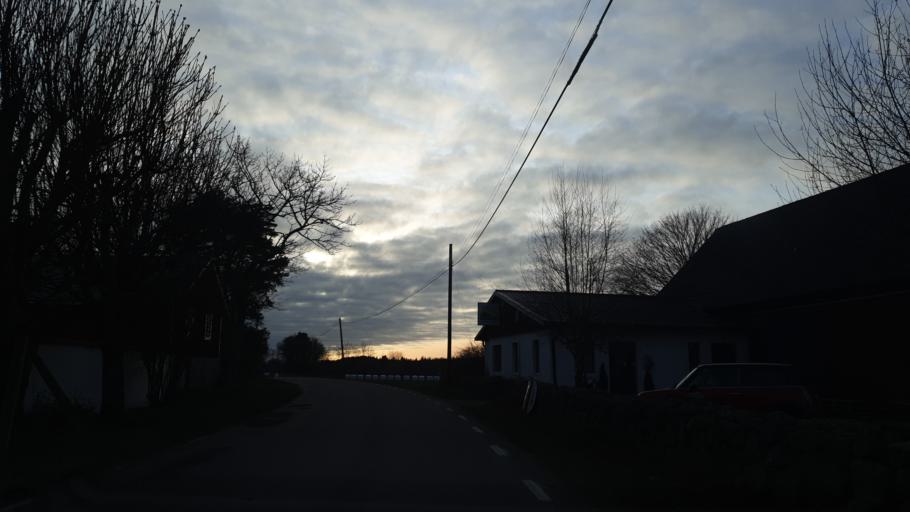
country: SE
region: Blekinge
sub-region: Karlskrona Kommun
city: Jaemjoe
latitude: 56.1892
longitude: 15.9456
